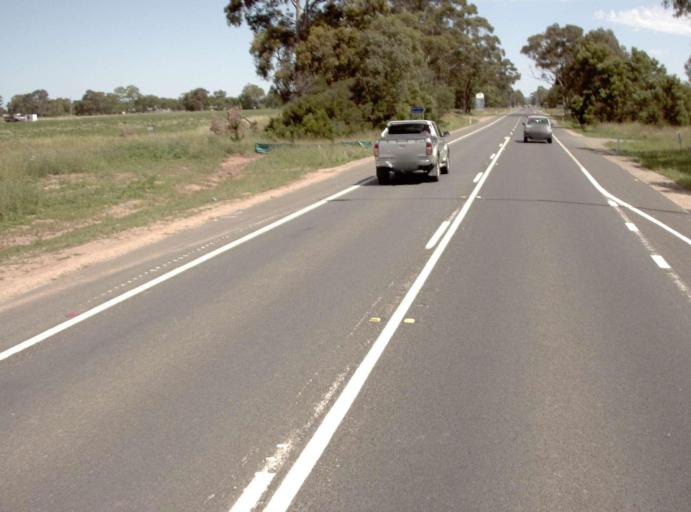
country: AU
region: Victoria
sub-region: Wellington
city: Sale
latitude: -38.0811
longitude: 147.0714
